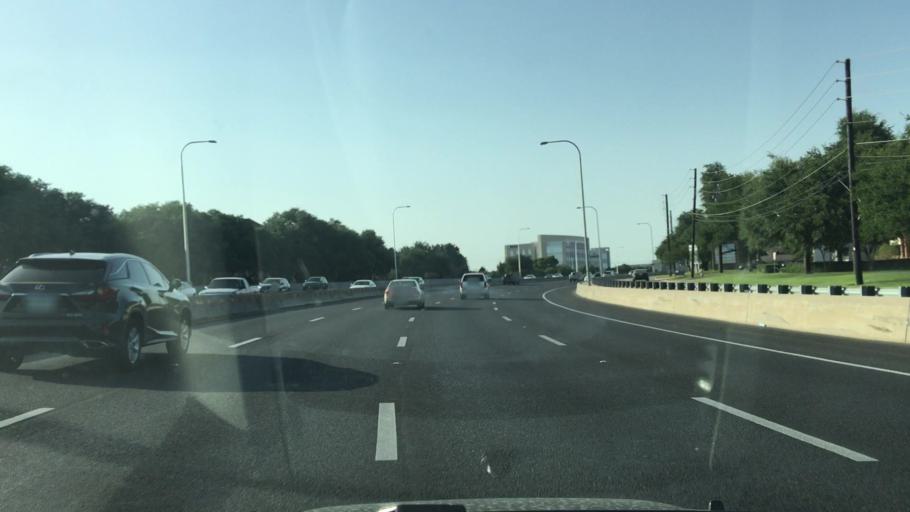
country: US
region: Texas
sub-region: Dallas County
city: Addison
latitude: 32.9798
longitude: -96.8283
